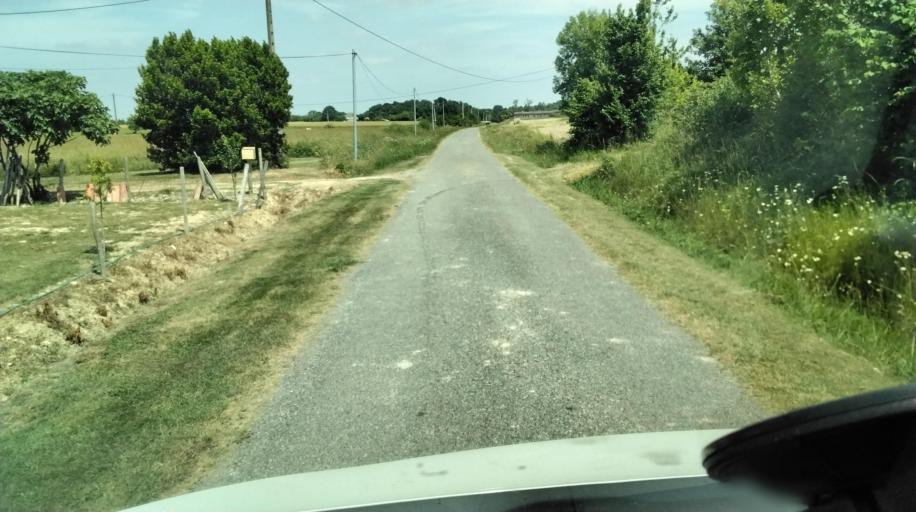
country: FR
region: Midi-Pyrenees
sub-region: Departement de la Haute-Garonne
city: Rieumes
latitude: 43.4007
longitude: 1.1052
